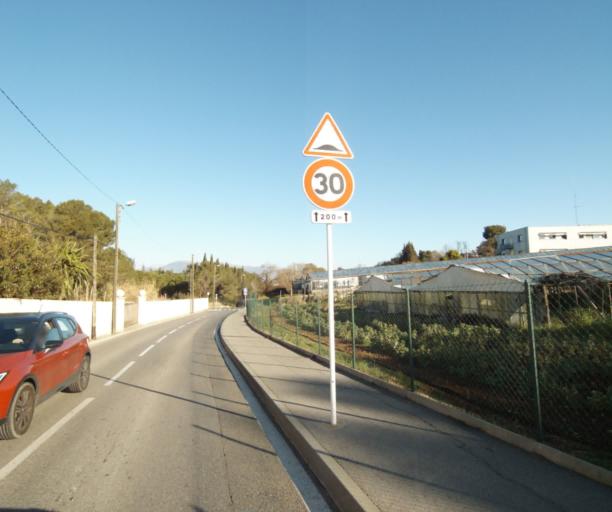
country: FR
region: Provence-Alpes-Cote d'Azur
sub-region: Departement des Alpes-Maritimes
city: Vallauris
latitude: 43.5980
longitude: 7.0759
